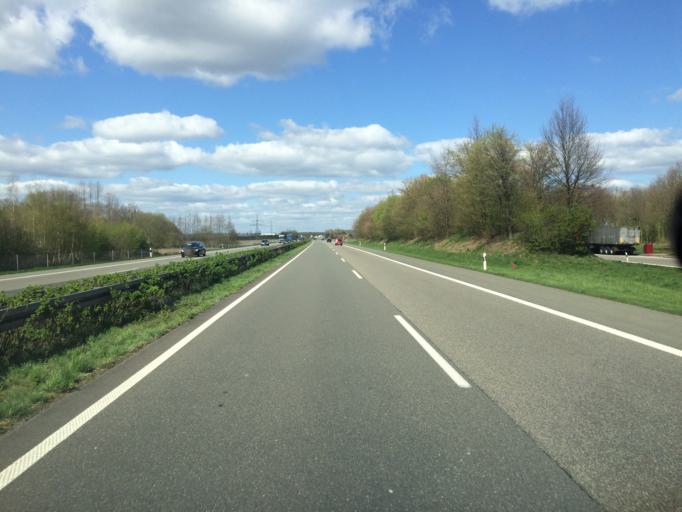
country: DE
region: North Rhine-Westphalia
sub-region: Regierungsbezirk Munster
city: Heek
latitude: 52.1023
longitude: 7.0859
